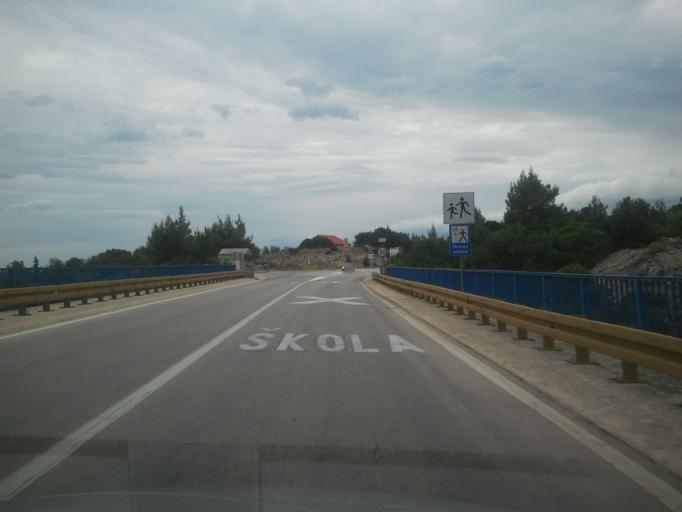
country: HR
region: Zadarska
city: Krusevo
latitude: 44.1300
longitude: 15.6358
